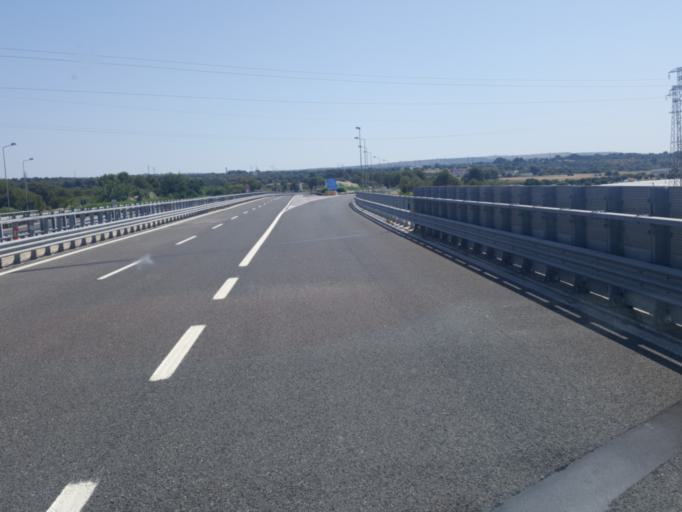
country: IT
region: Apulia
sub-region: Provincia di Taranto
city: Massafra
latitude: 40.5958
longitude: 17.0790
